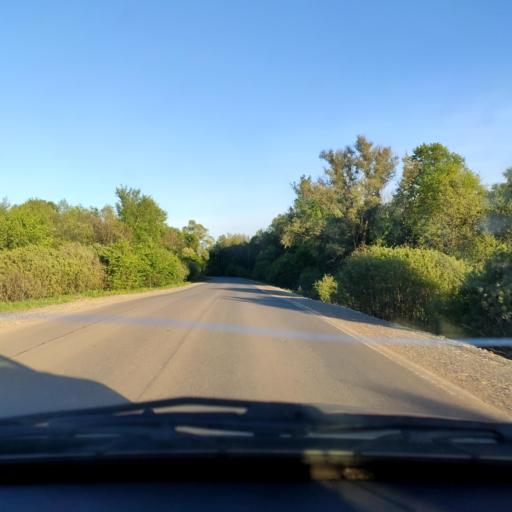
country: RU
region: Bashkortostan
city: Yazykovo
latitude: 55.0275
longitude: 56.2076
